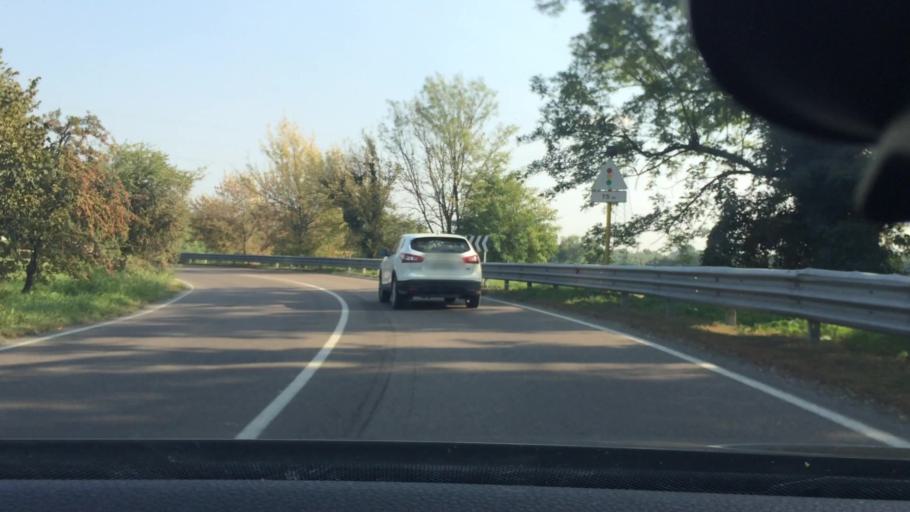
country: IT
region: Lombardy
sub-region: Citta metropolitana di Milano
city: Figino
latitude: 45.5009
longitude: 9.0693
